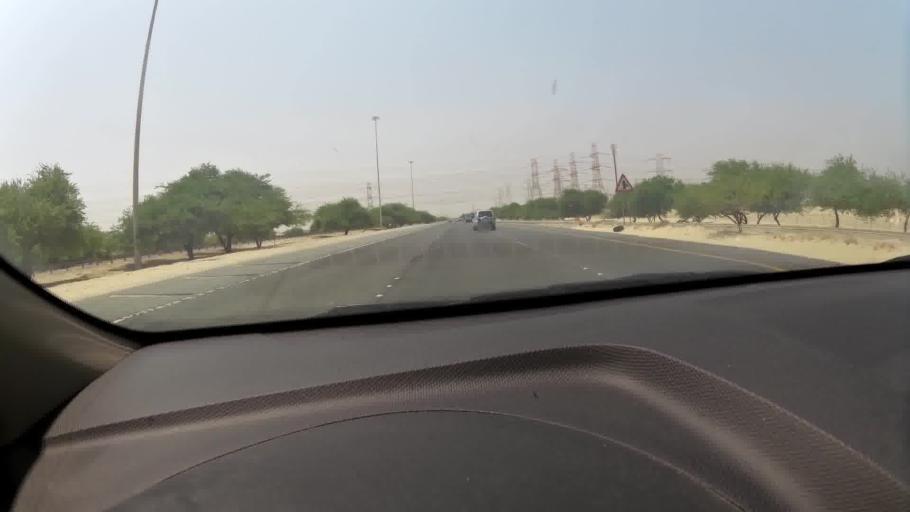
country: KW
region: Al Ahmadi
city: Al Fahahil
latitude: 28.9320
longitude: 48.1778
